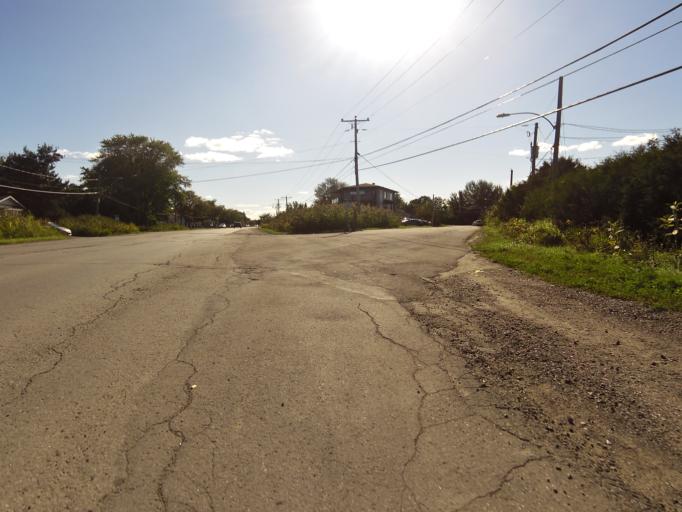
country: CA
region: Quebec
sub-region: Outaouais
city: Gatineau
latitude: 45.5021
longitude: -75.5649
